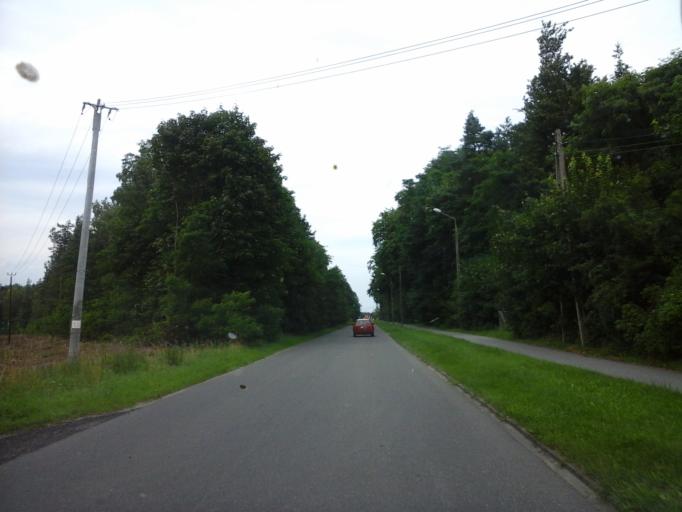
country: PL
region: West Pomeranian Voivodeship
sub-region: Powiat choszczenski
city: Bierzwnik
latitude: 53.0254
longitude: 15.6608
